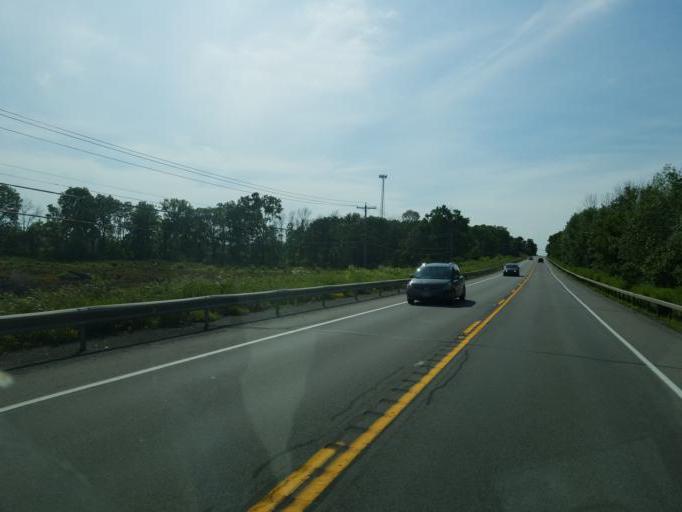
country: US
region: New York
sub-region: Livingston County
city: Avon
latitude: 42.9244
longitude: -77.7732
